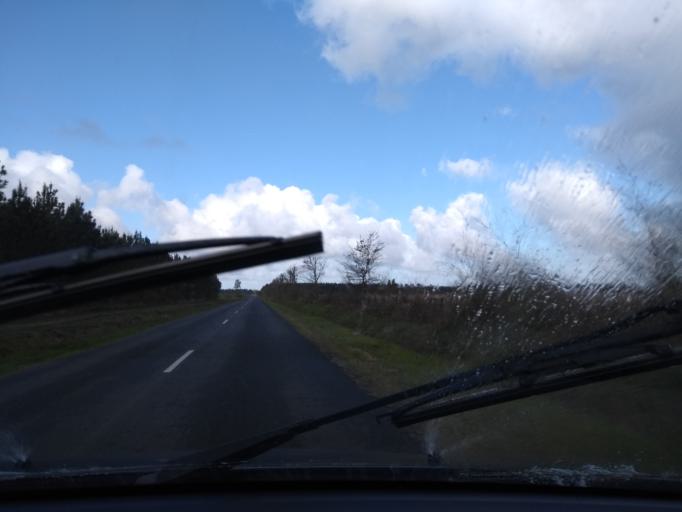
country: FR
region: Aquitaine
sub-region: Departement de la Gironde
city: Mios
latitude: 44.5506
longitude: -0.9587
